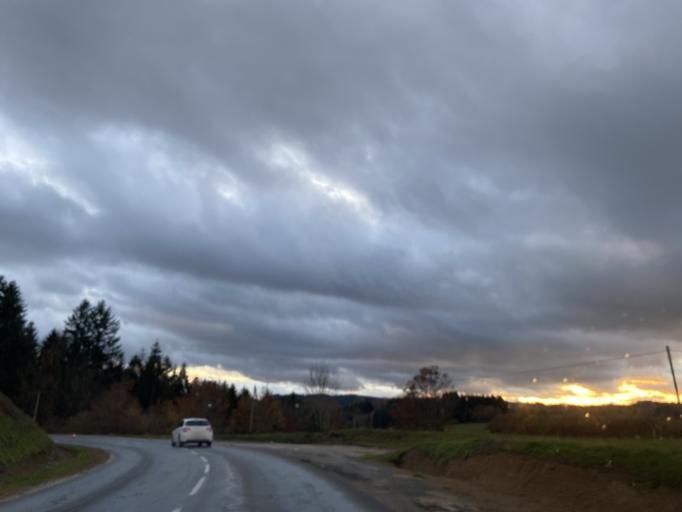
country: FR
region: Auvergne
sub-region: Departement du Puy-de-Dome
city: Cunlhat
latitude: 45.6533
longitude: 3.5599
